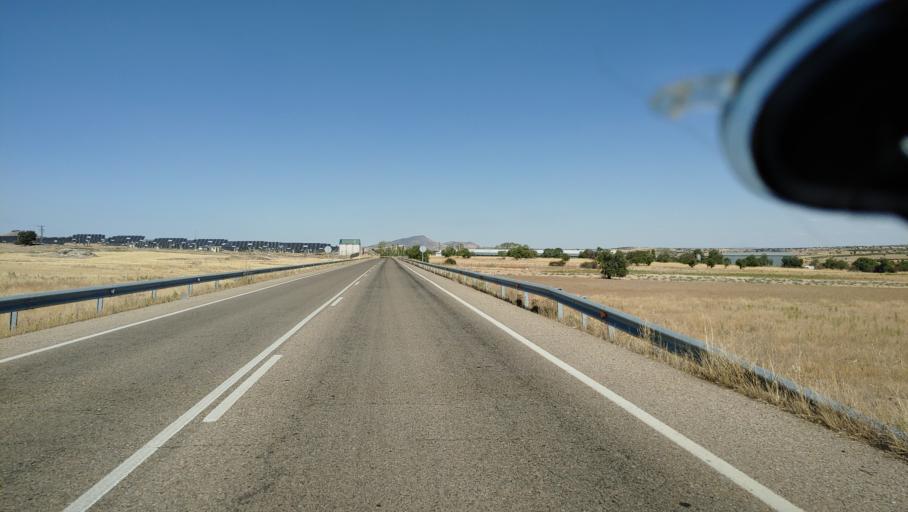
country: ES
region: Castille-La Mancha
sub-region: Province of Toledo
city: Cuerva
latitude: 39.6702
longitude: -4.1972
